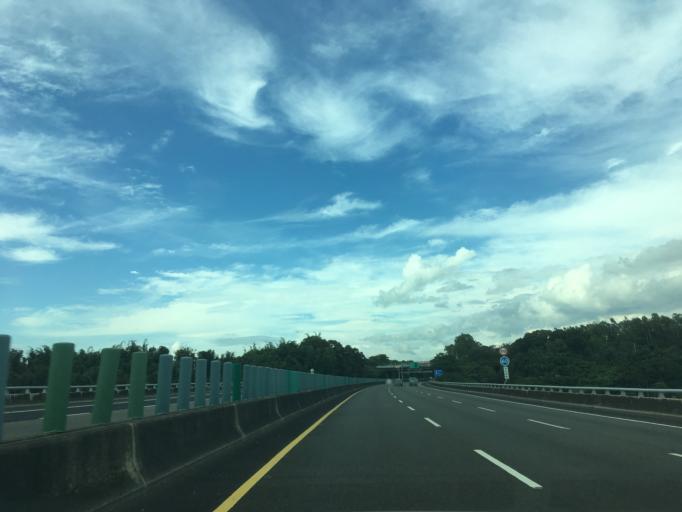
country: TW
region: Taiwan
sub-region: Yunlin
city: Douliu
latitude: 23.6040
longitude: 120.5287
